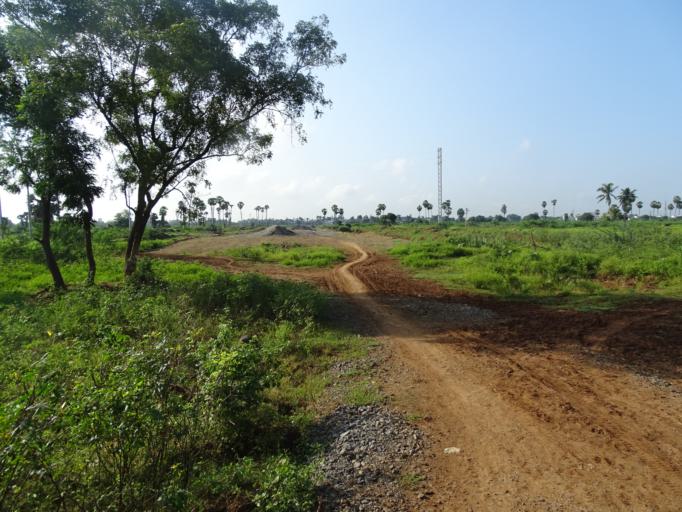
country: IN
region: Andhra Pradesh
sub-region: Guntur
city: Mangalagiri
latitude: 16.4423
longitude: 80.5335
